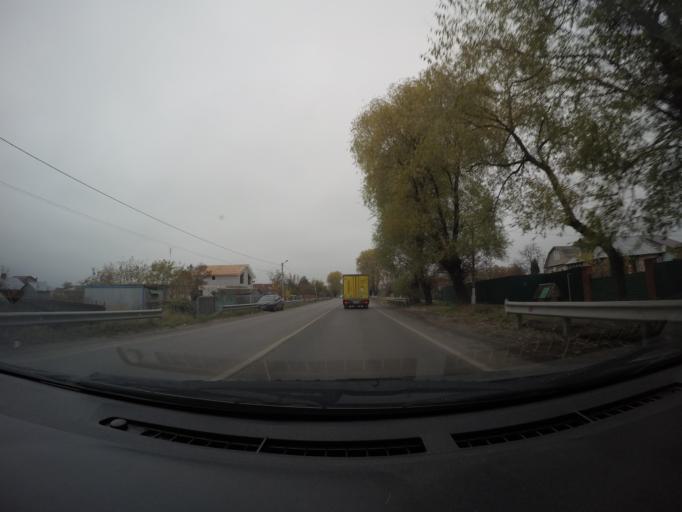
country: RU
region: Moskovskaya
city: Rechitsy
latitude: 55.6025
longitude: 38.4459
